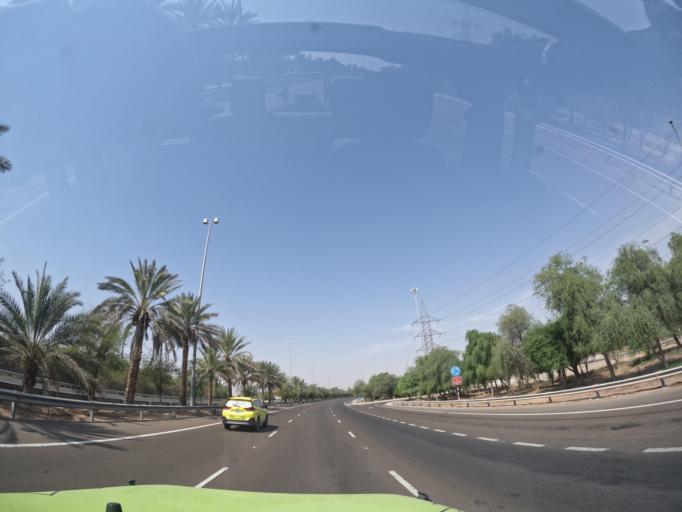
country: AE
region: Abu Dhabi
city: Al Ain
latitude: 24.2101
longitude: 55.5133
